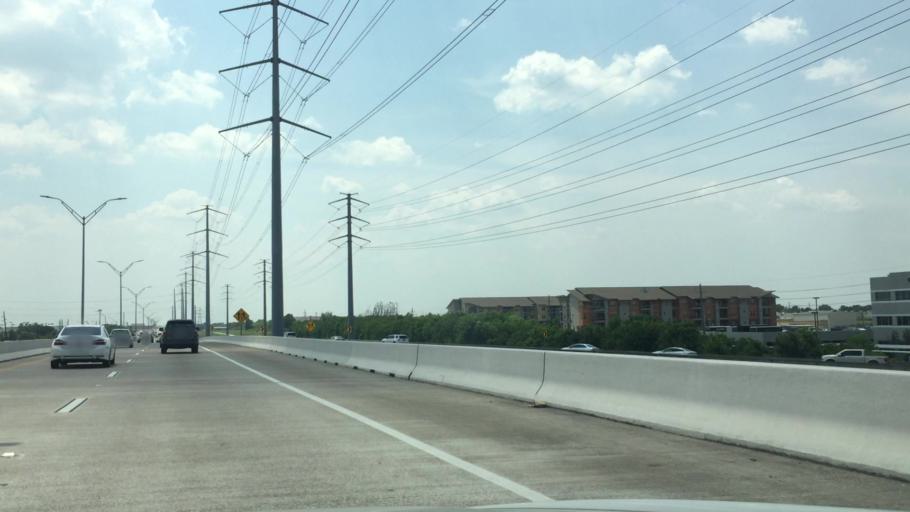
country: US
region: Texas
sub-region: Harris County
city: Bunker Hill Village
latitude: 29.7182
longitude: -95.5595
